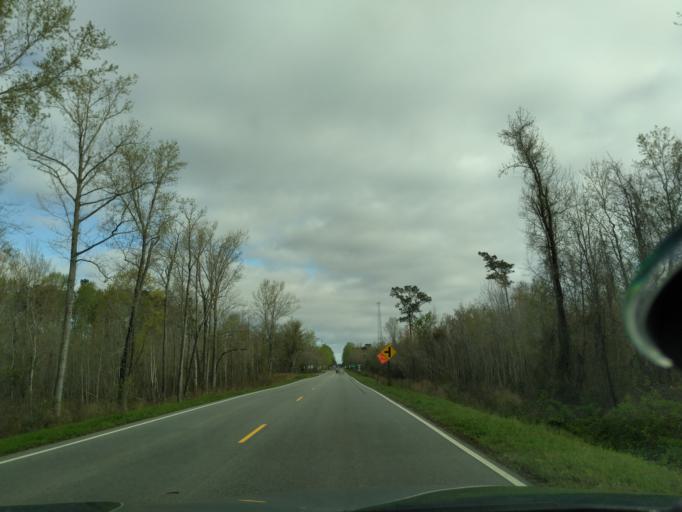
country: US
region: North Carolina
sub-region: Washington County
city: Plymouth
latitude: 35.9349
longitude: -76.7424
